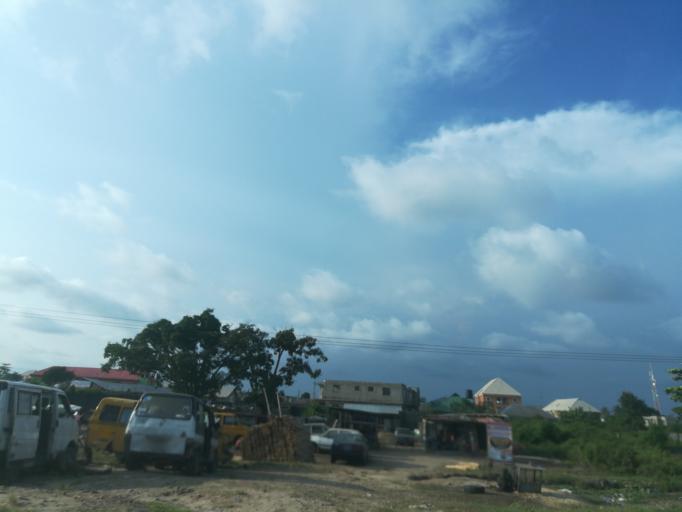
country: NG
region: Ogun
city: Ado Odo
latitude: 6.4827
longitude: 3.0370
